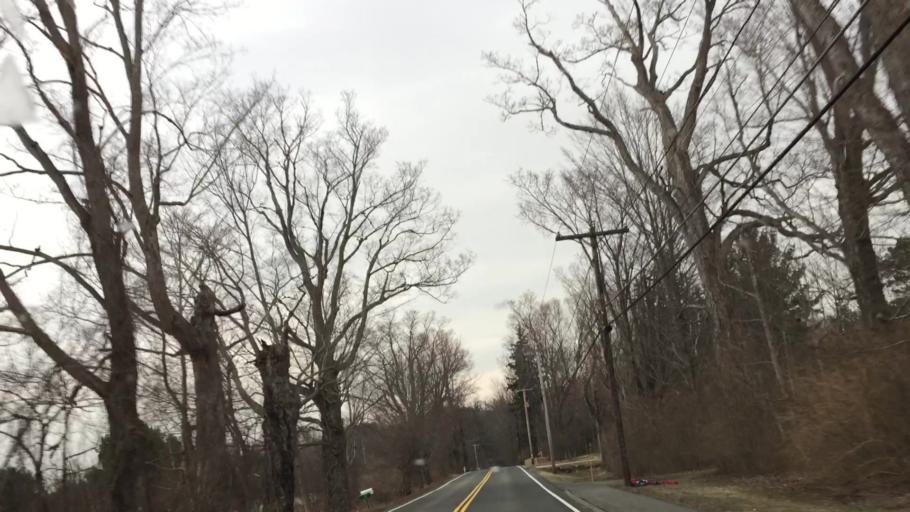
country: US
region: Massachusetts
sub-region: Berkshire County
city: Lenox
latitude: 42.3441
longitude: -73.2550
